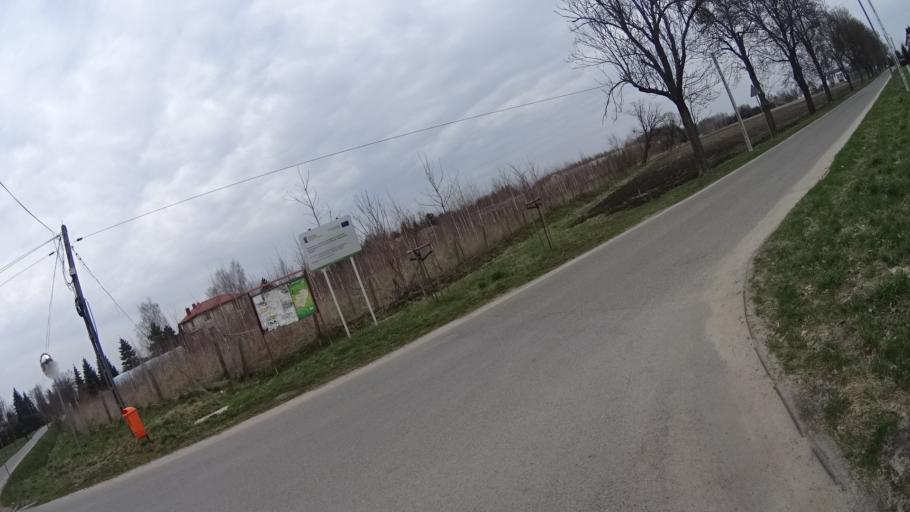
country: PL
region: Masovian Voivodeship
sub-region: Powiat warszawski zachodni
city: Jozefow
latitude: 52.2063
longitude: 20.6836
